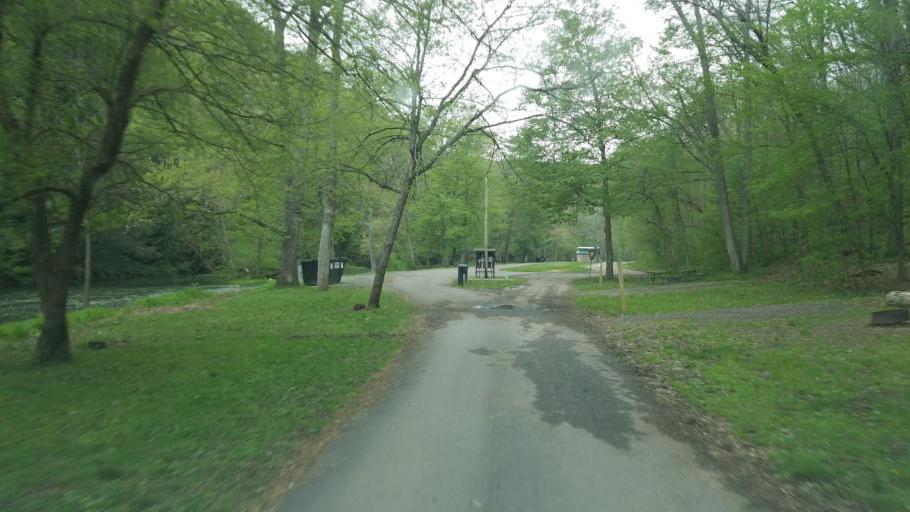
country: US
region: Ohio
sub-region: Ashland County
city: Loudonville
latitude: 40.6120
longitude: -82.3118
